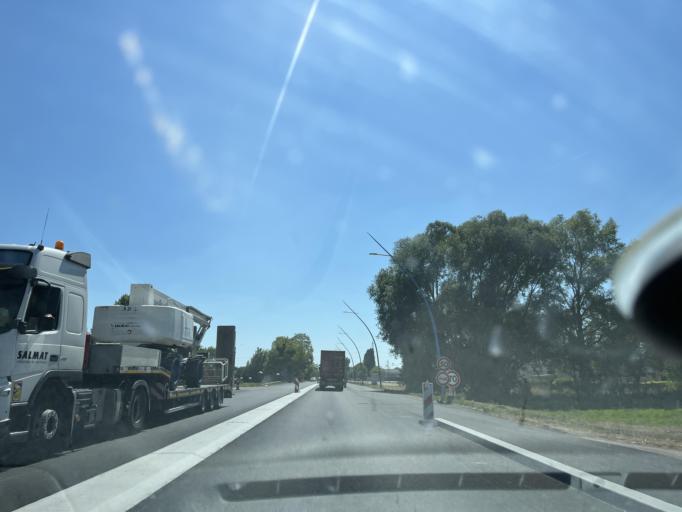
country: FR
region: Haute-Normandie
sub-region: Departement de la Seine-Maritime
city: Lillebonne
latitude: 49.4989
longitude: 0.5358
